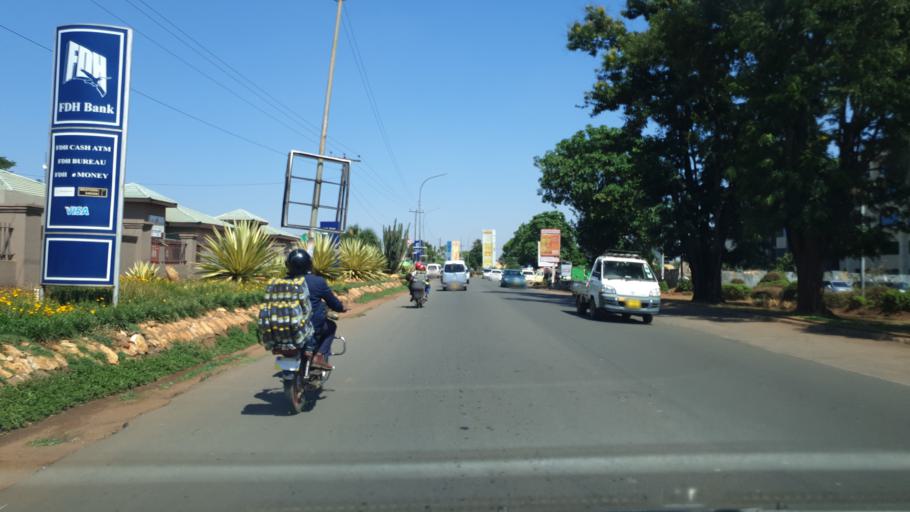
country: MW
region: Central Region
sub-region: Lilongwe District
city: Lilongwe
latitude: -13.9758
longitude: 33.7581
